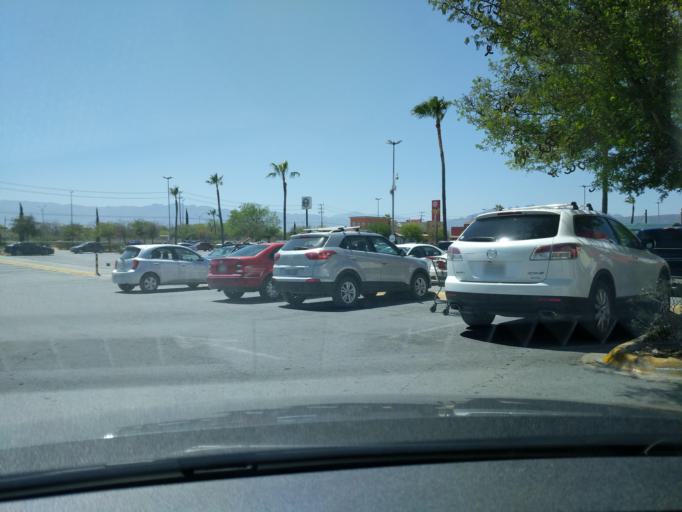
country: MX
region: Nuevo Leon
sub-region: Apodaca
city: Fraccionamiento Cosmopolis Octavo Sector
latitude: 25.7851
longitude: -100.2260
